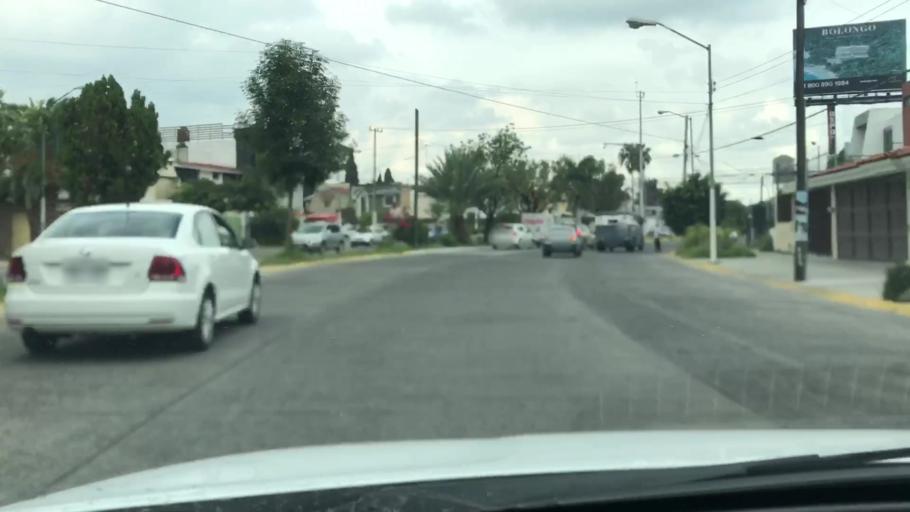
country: MX
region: Jalisco
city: Guadalajara
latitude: 20.6406
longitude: -103.4327
